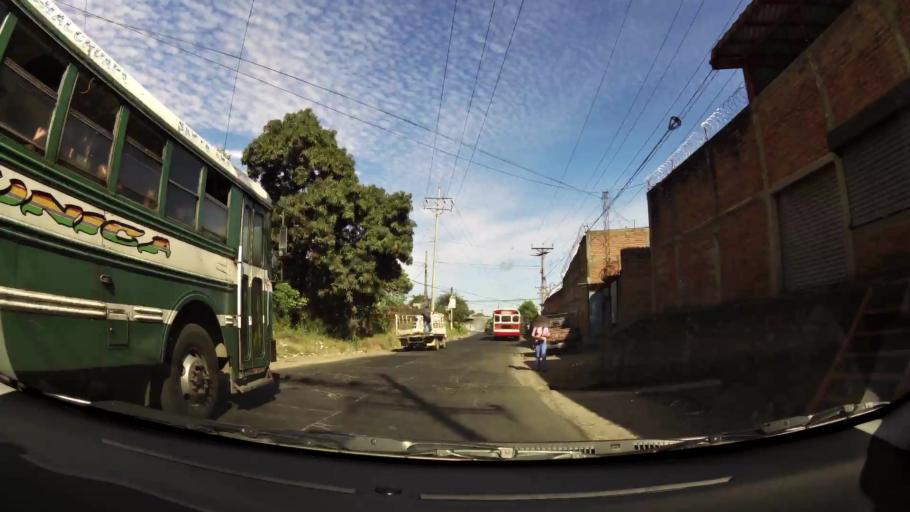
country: SV
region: Santa Ana
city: Santa Ana
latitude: 13.9817
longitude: -89.5795
